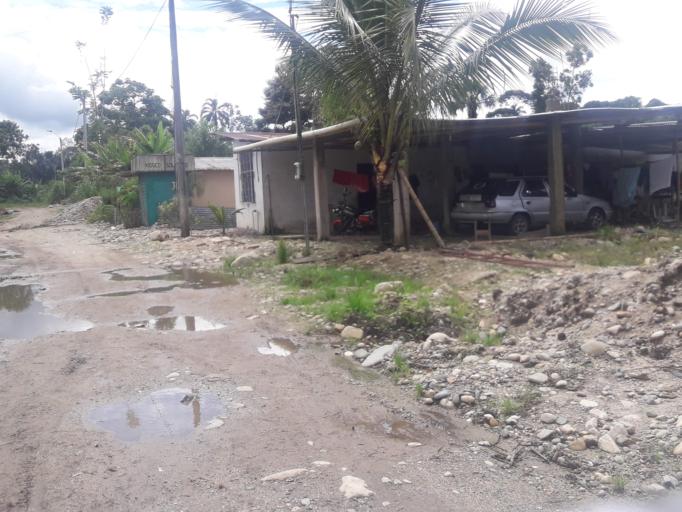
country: EC
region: Napo
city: Tena
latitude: -0.9786
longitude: -77.8516
